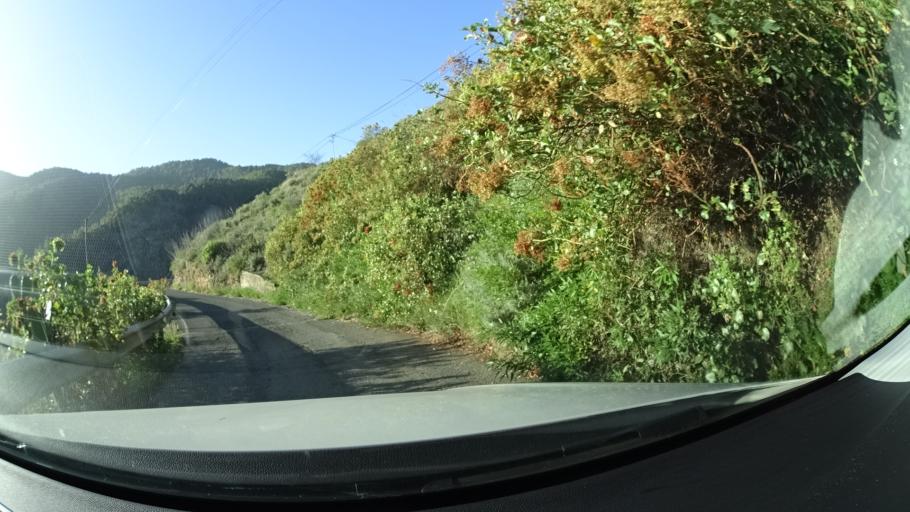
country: ES
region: Canary Islands
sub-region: Provincia de Las Palmas
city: Artenara
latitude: 28.0486
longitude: -15.6665
